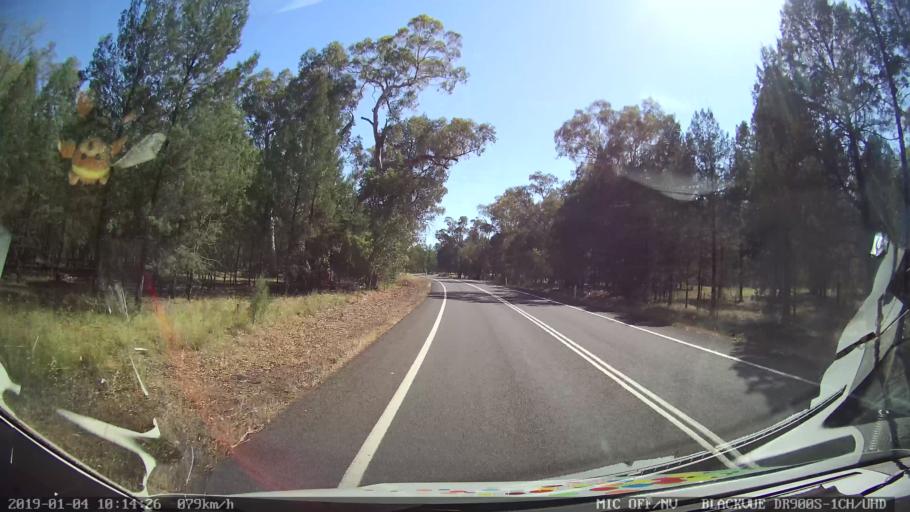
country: AU
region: New South Wales
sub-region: Cabonne
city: Canowindra
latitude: -33.3970
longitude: 148.4135
